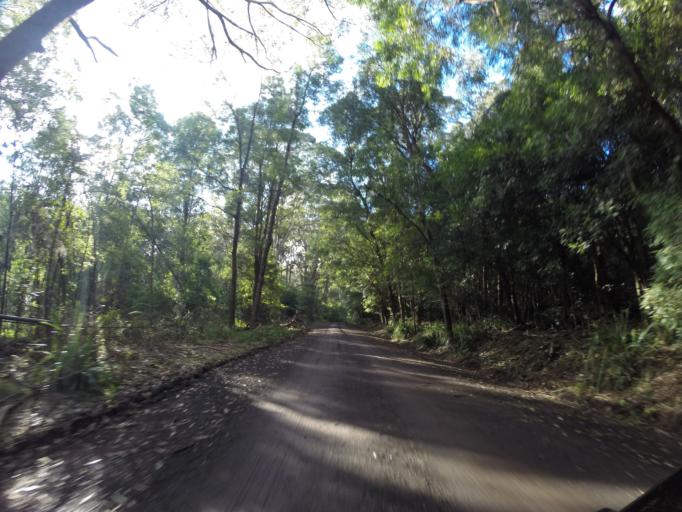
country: AU
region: New South Wales
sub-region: Wollongong
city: Cordeaux Heights
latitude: -34.4204
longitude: 150.7837
